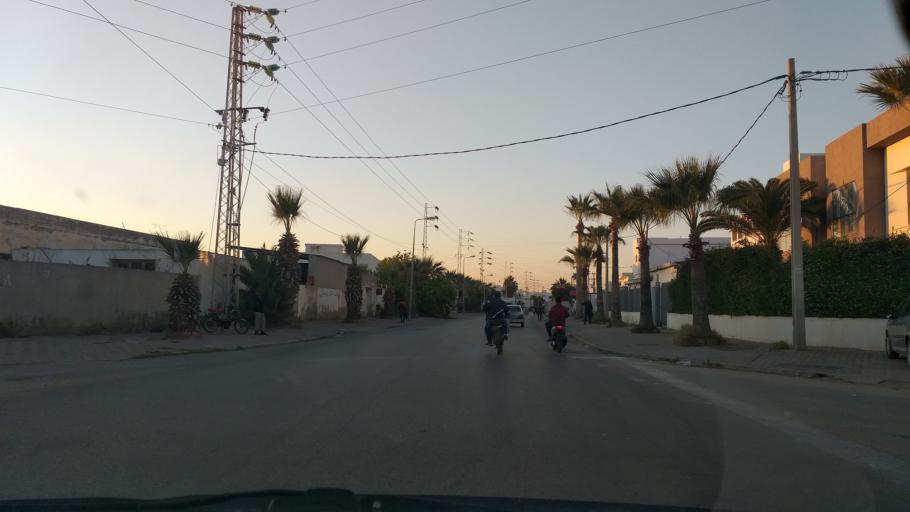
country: TN
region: Safaqis
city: Al Qarmadah
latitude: 34.7611
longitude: 10.7785
